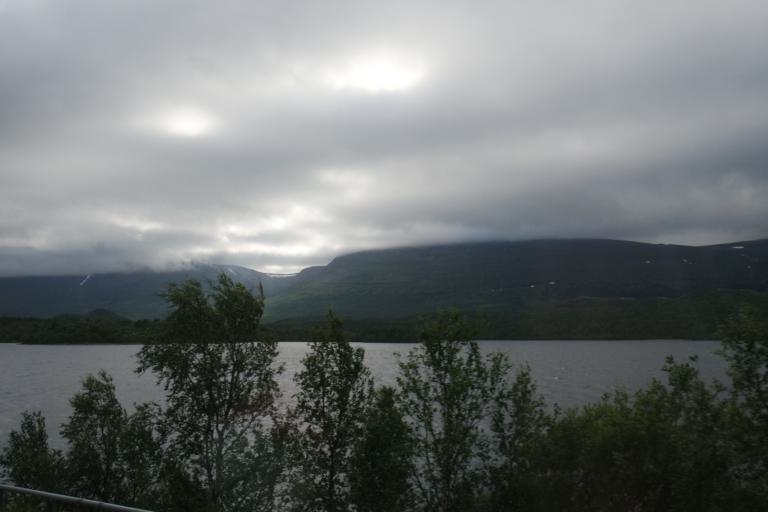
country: NO
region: Finnmark Fylke
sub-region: Porsanger
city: Lakselv
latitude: 69.8922
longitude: 24.9961
